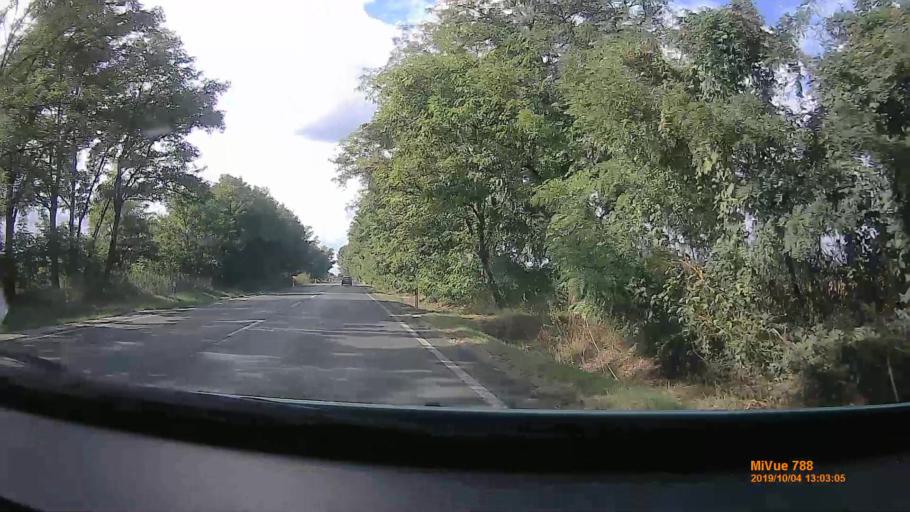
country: HU
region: Szabolcs-Szatmar-Bereg
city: Nyirtelek
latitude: 47.9577
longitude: 21.6408
